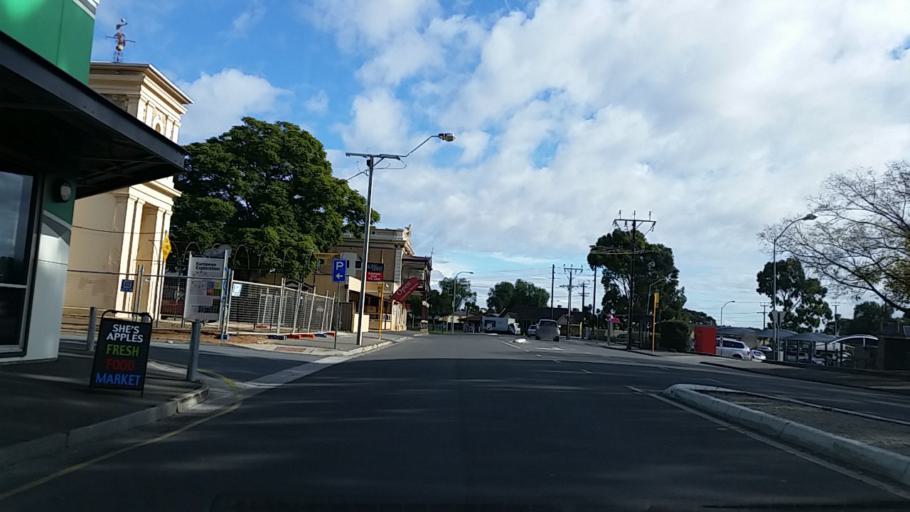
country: AU
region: South Australia
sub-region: Gawler
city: Gawler
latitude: -34.5960
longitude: 138.7485
